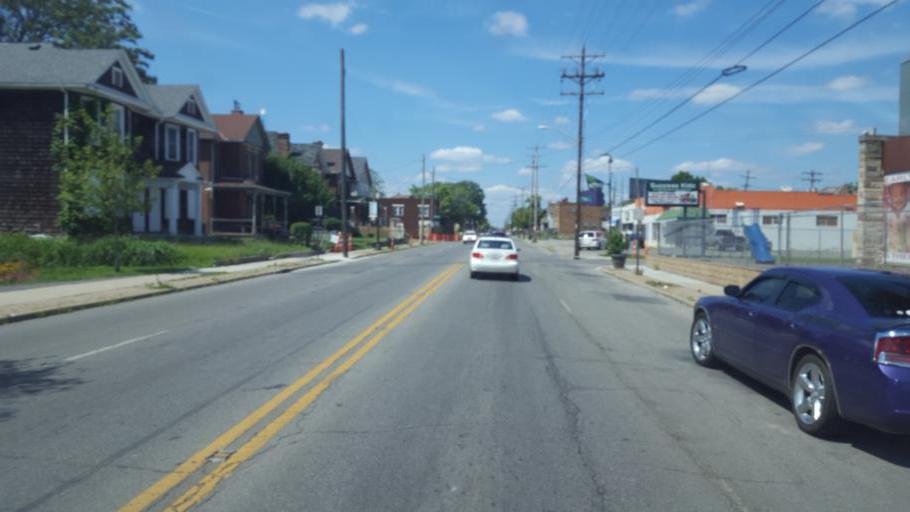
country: US
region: Ohio
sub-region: Franklin County
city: Columbus
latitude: 39.9262
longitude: -82.9843
